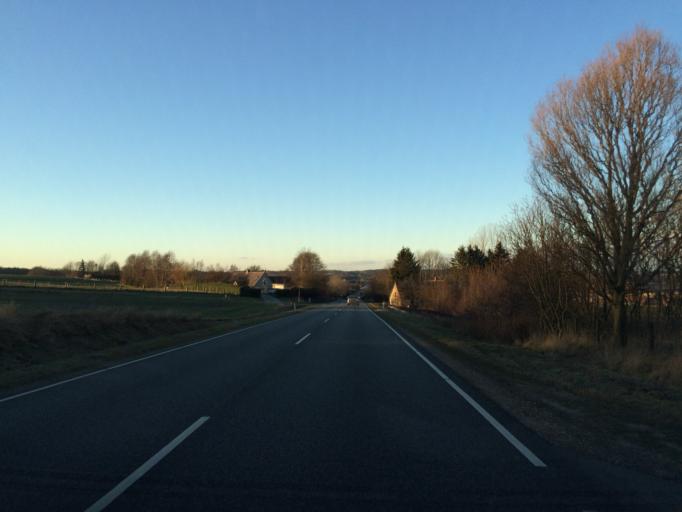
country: DK
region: Central Jutland
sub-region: Randers Kommune
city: Langa
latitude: 56.4835
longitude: 9.8729
